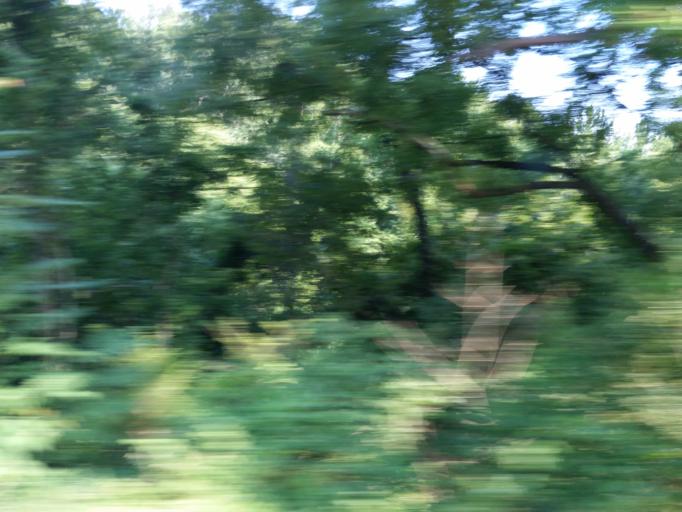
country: US
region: Tennessee
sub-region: Blount County
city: Eagleton Village
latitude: 35.8531
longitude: -83.9170
